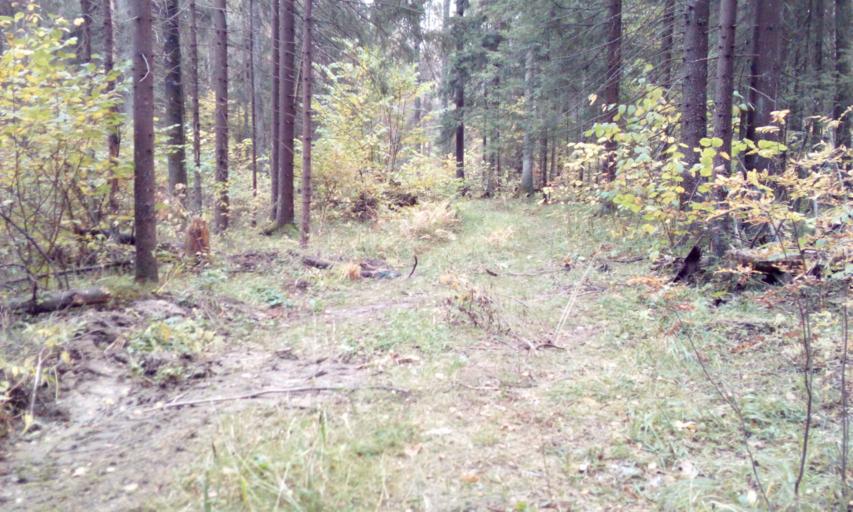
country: RU
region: Moskovskaya
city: Selyatino
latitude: 55.4862
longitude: 36.9635
